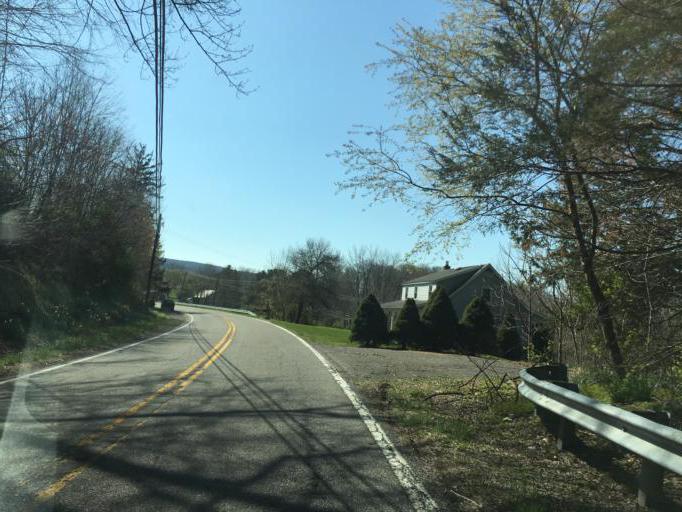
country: US
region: Maryland
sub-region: Frederick County
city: Myersville
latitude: 39.5665
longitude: -77.5308
